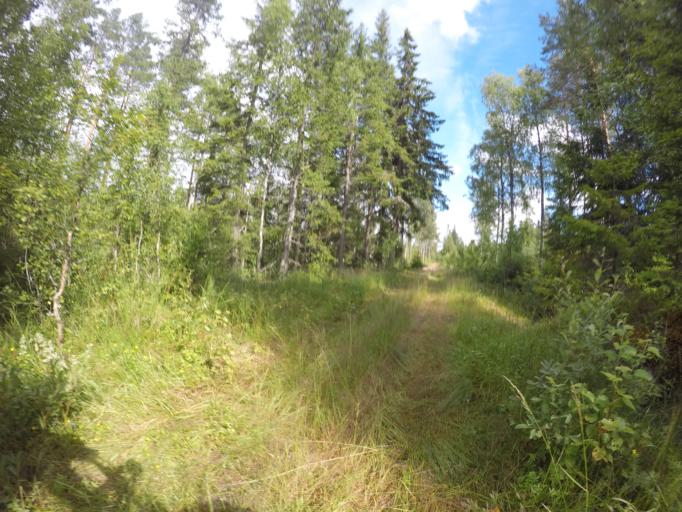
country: SE
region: OErebro
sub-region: Hallefors Kommun
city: Haellefors
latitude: 60.0346
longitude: 14.5375
